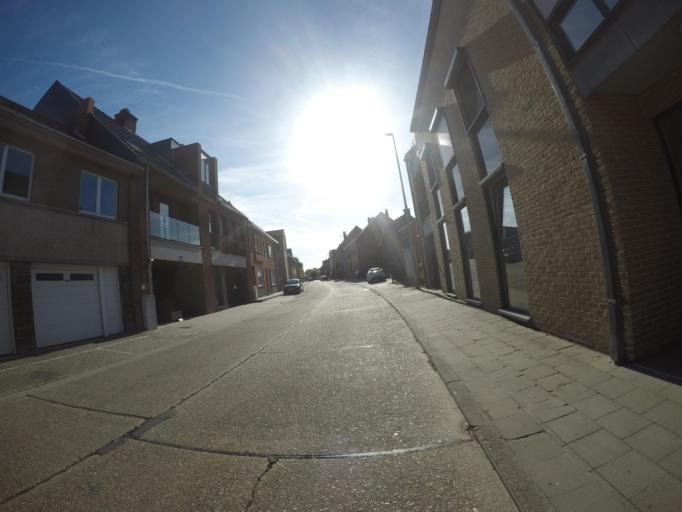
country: BE
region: Flanders
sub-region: Provincie Limburg
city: Diepenbeek
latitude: 50.9092
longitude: 5.4174
